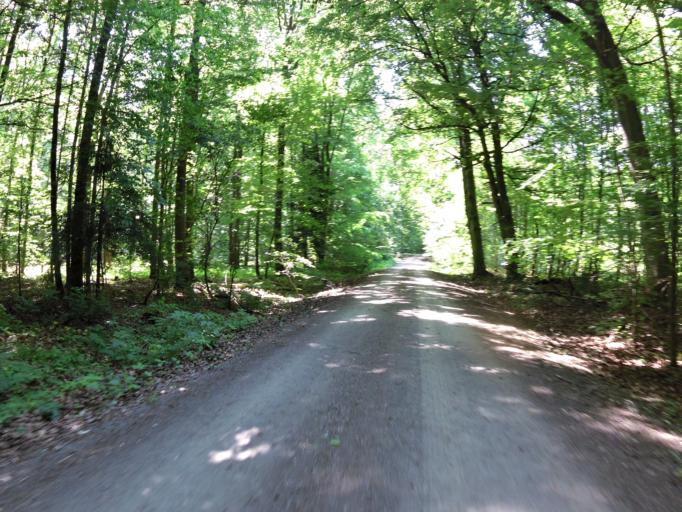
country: DE
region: Bavaria
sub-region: Regierungsbezirk Unterfranken
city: Kleinrinderfeld
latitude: 49.7210
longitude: 9.8633
